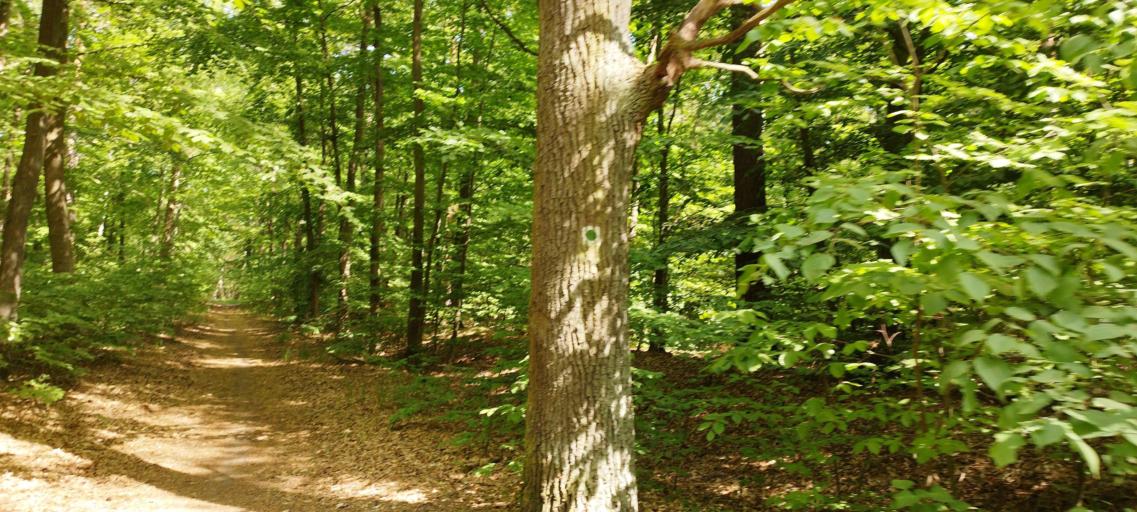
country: DE
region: Brandenburg
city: Furstenwalde
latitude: 52.3687
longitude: 14.0377
